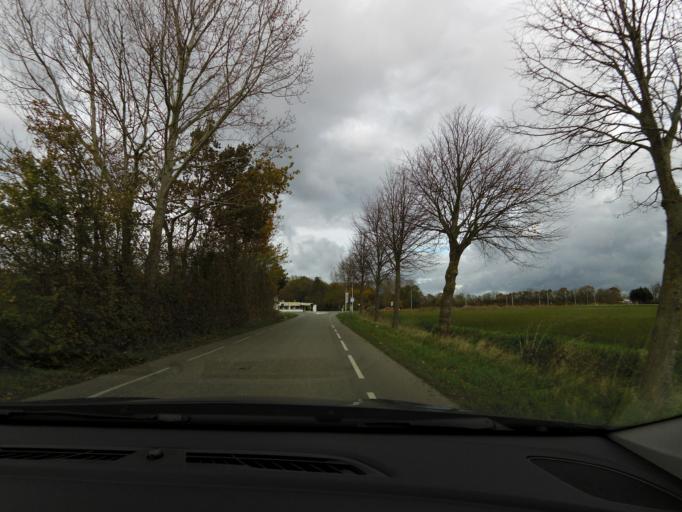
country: NL
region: Zeeland
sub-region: Schouwen-Duiveland
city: Bruinisse
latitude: 51.6562
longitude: 4.0443
